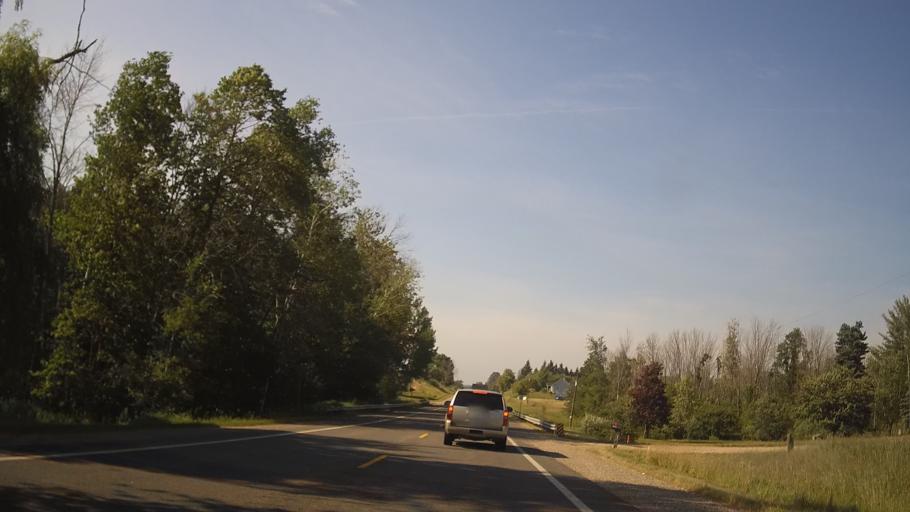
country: US
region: Michigan
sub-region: Ogemaw County
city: West Branch
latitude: 44.3739
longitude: -84.1159
